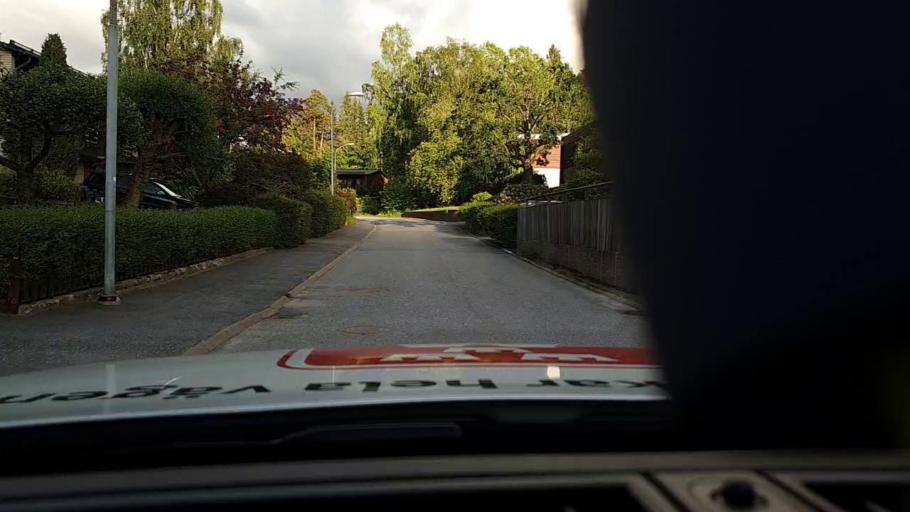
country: SE
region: Stockholm
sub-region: Huddinge Kommun
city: Huddinge
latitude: 59.2472
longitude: 17.9653
